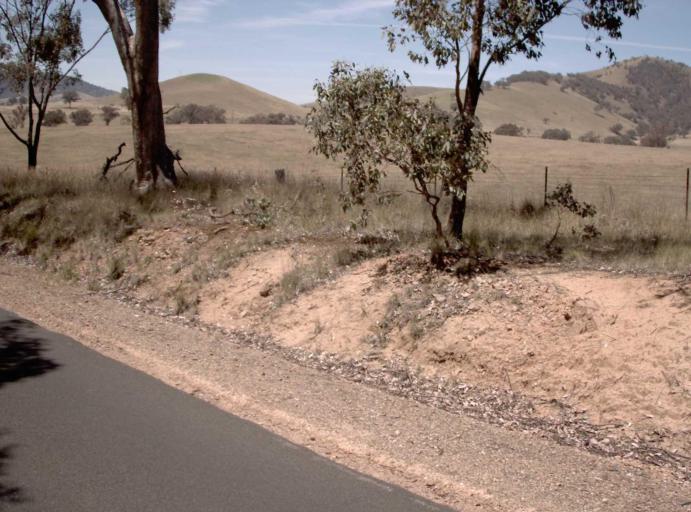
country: AU
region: Victoria
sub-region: East Gippsland
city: Bairnsdale
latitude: -37.1757
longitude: 147.7006
